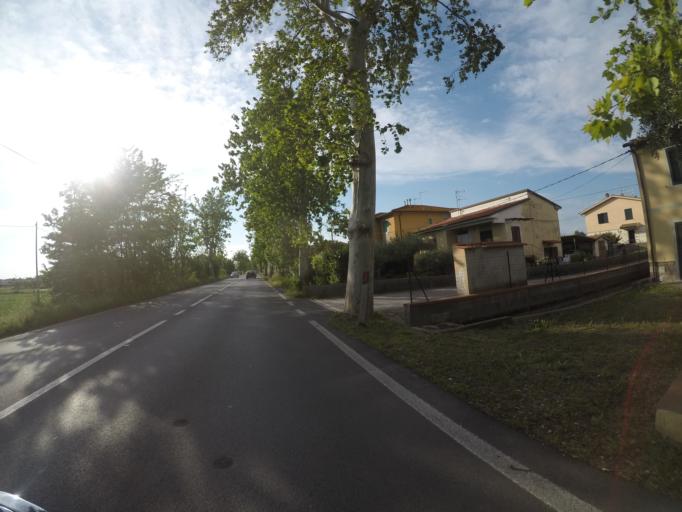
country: IT
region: Tuscany
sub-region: Province of Pisa
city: Madonna dell'Acqua
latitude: 43.7463
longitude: 10.3680
